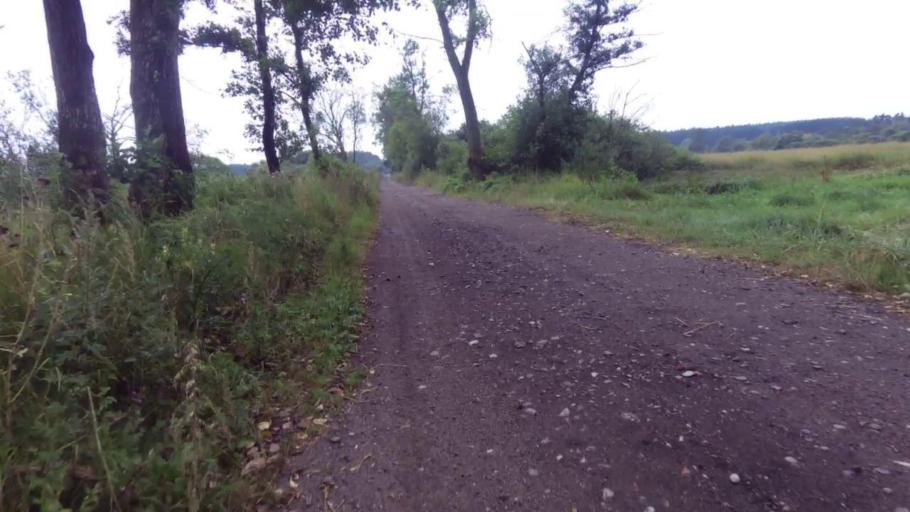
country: PL
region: West Pomeranian Voivodeship
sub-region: Powiat stargardzki
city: Suchan
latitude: 53.2496
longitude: 15.3842
